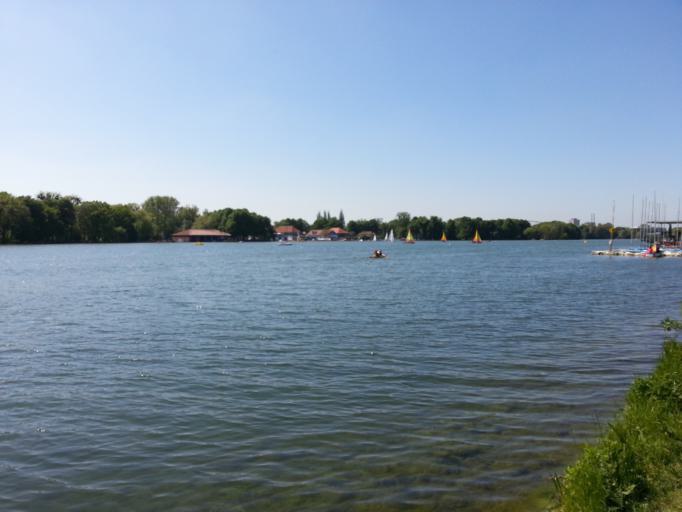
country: DE
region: Lower Saxony
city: Hannover
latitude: 52.3529
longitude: 9.7470
